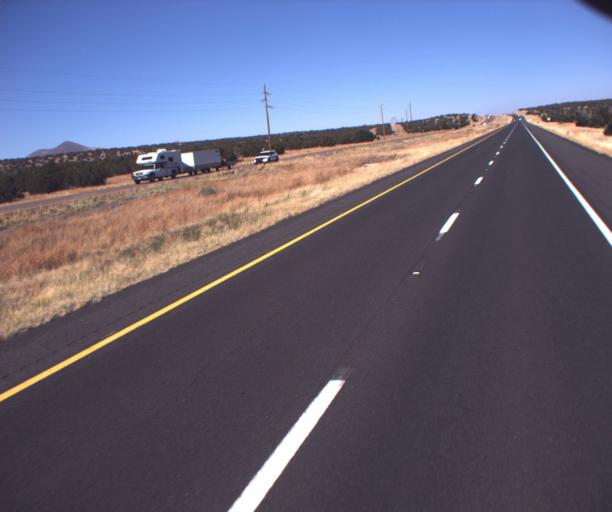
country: US
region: Arizona
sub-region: Coconino County
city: Flagstaff
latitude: 35.4606
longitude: -111.5603
